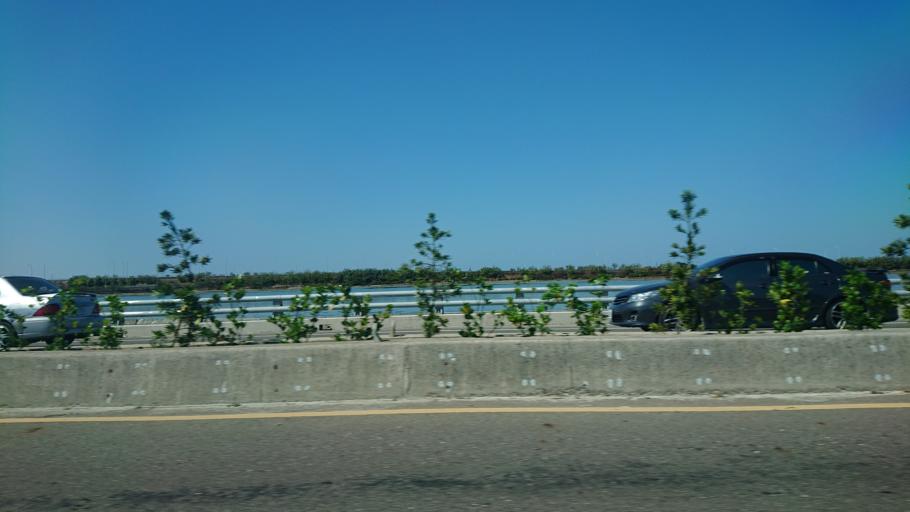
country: TW
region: Taiwan
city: Xinying
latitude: 23.2805
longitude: 120.1318
